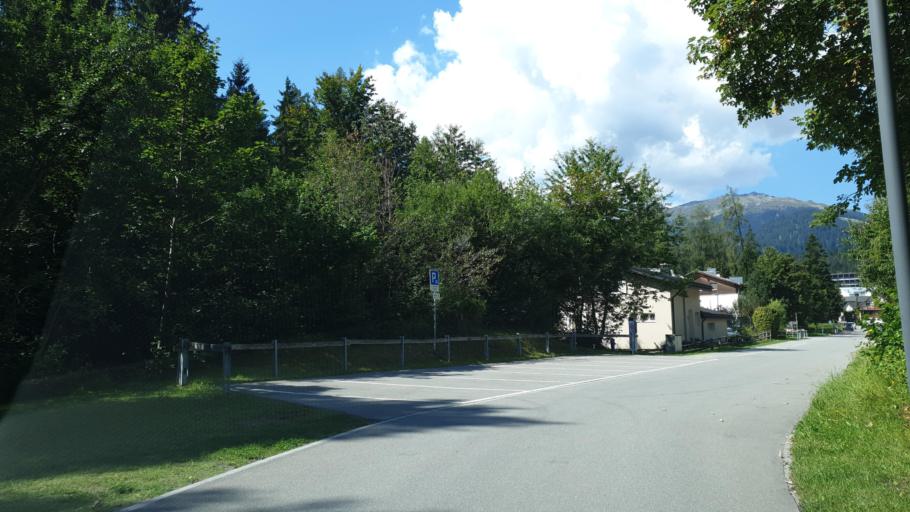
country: CH
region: Grisons
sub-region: Imboden District
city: Flims
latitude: 46.8272
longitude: 9.2930
